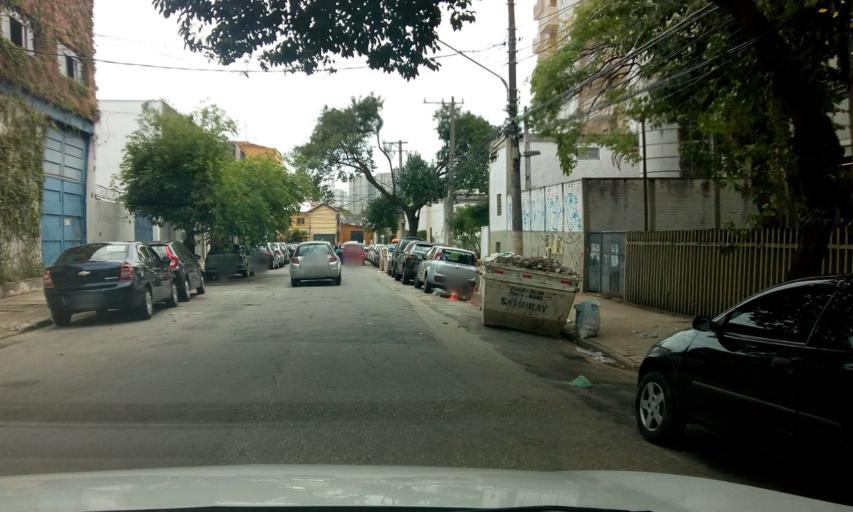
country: BR
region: Sao Paulo
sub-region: Sao Paulo
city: Sao Paulo
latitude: -23.5286
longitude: -46.6559
